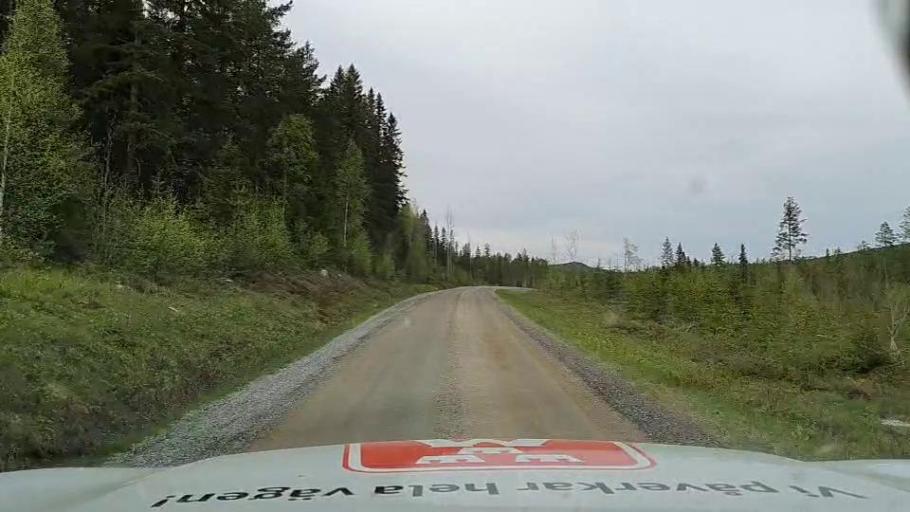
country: SE
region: Jaemtland
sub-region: Bergs Kommun
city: Hoverberg
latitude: 62.5464
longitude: 14.8982
